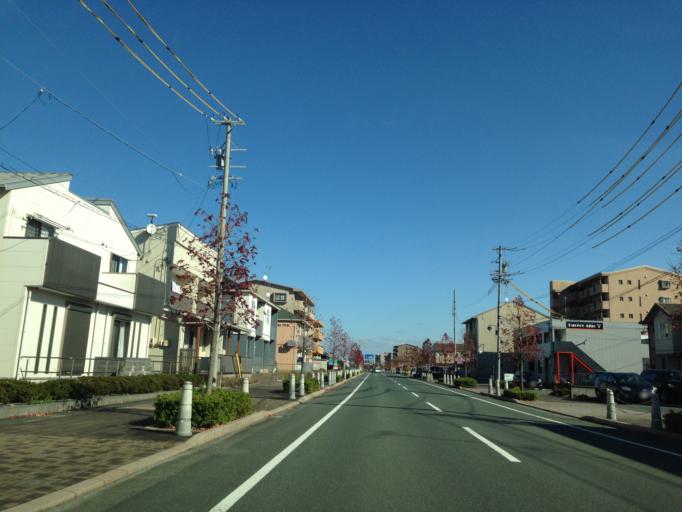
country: JP
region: Shizuoka
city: Fukuroi
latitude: 34.7514
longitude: 137.9557
